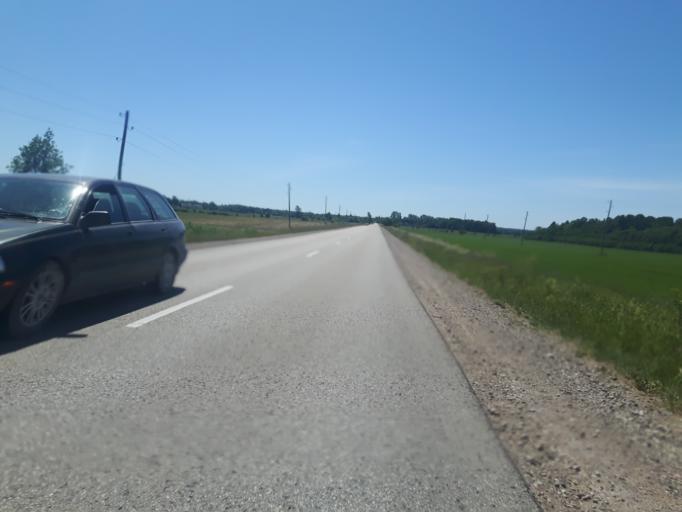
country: LV
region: Durbe
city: Liegi
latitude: 56.5757
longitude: 21.2704
